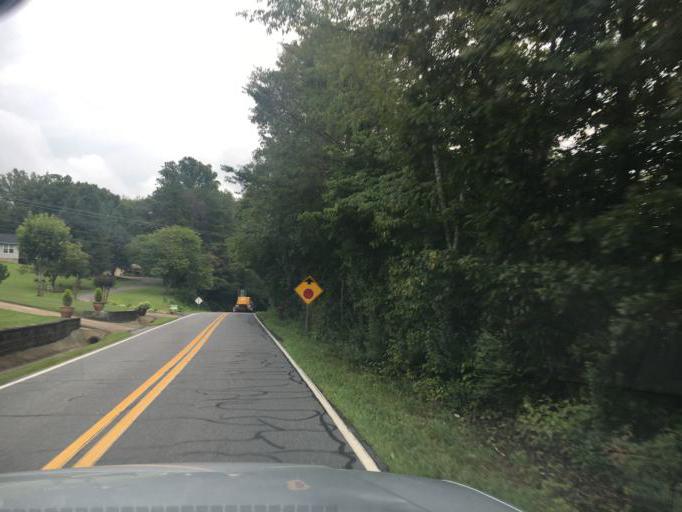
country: US
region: North Carolina
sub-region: McDowell County
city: West Marion
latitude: 35.6272
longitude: -81.9886
